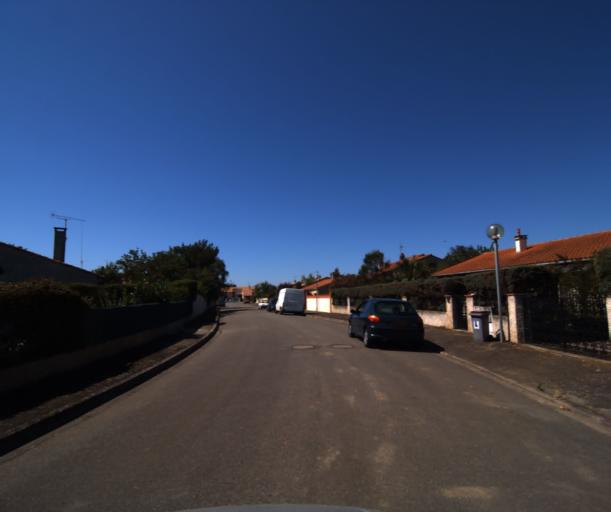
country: FR
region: Midi-Pyrenees
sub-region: Departement de la Haute-Garonne
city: Muret
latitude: 43.4714
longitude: 1.3223
